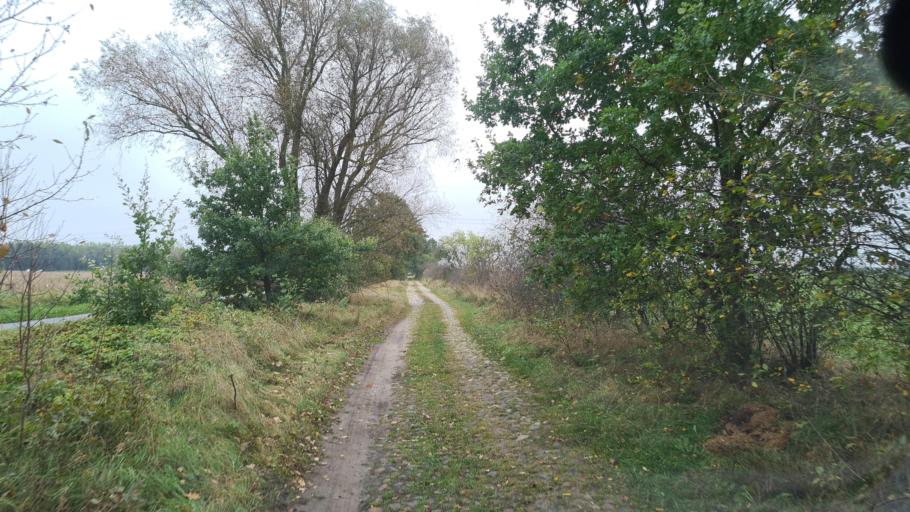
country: DE
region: Brandenburg
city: Furstenwalde
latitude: 52.4231
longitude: 14.0245
